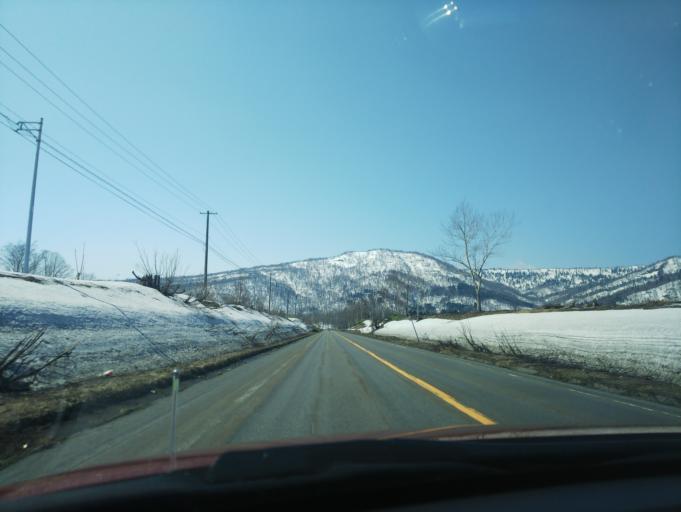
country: JP
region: Hokkaido
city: Nayoro
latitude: 44.6524
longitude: 142.2670
